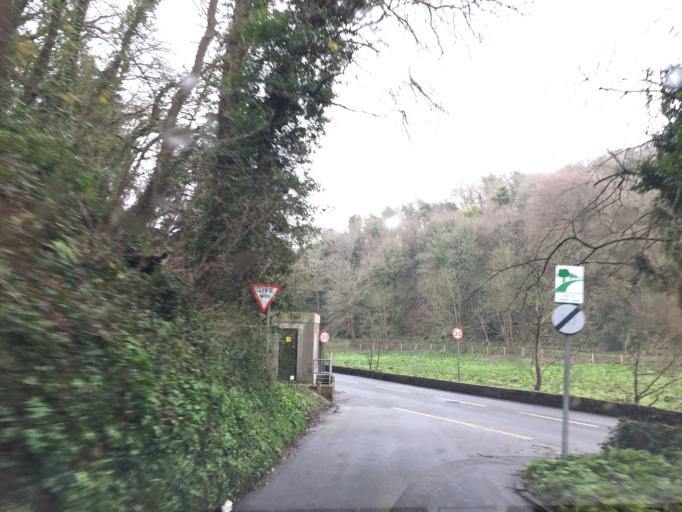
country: JE
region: St Helier
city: Saint Helier
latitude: 49.2103
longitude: -2.1612
